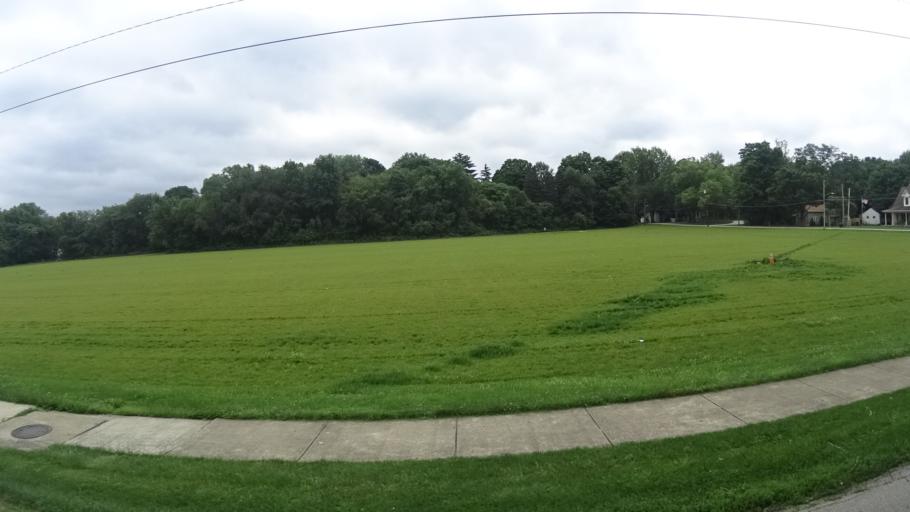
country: US
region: Indiana
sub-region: Madison County
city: Pendleton
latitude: 40.0044
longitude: -85.7416
